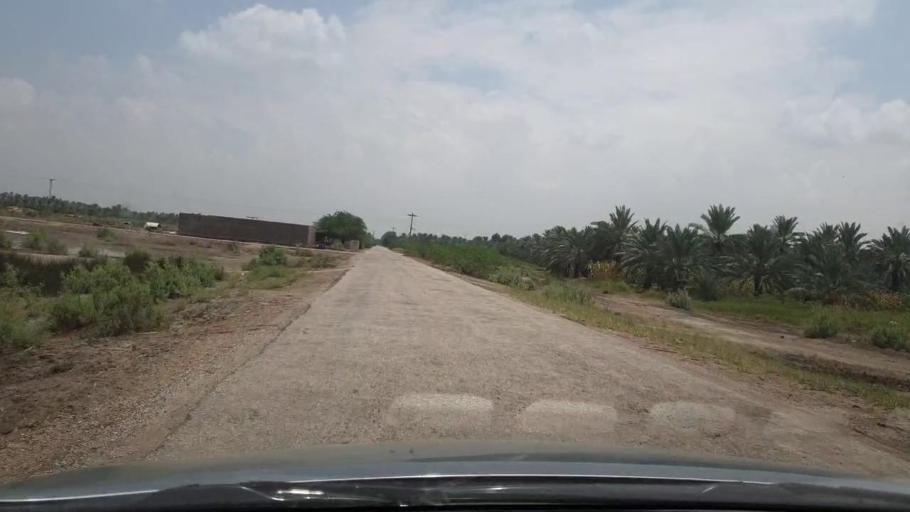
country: PK
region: Sindh
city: Khairpur
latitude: 27.4383
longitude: 68.7518
